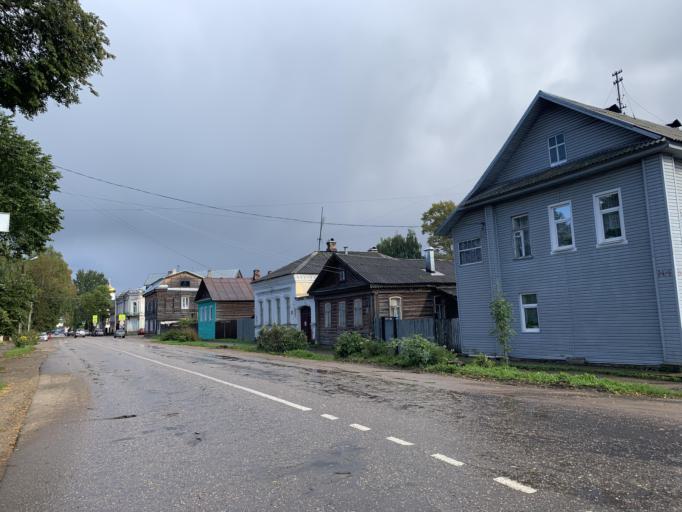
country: RU
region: Tverskaya
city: Vyshniy Volochek
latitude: 57.5839
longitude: 34.5498
